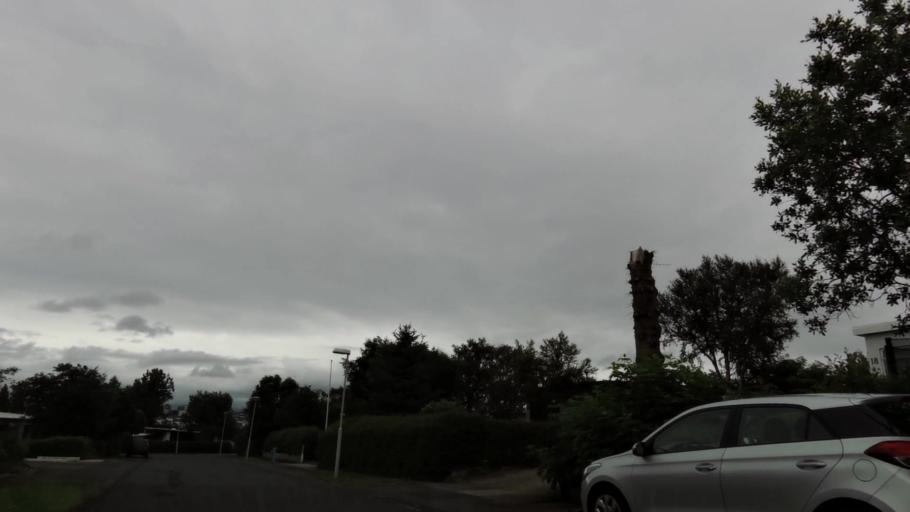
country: IS
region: Capital Region
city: Gardabaer
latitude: 64.0934
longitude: -21.9200
